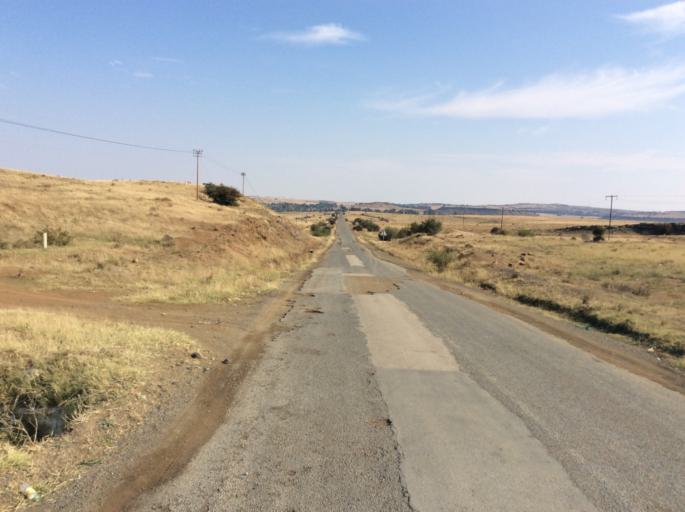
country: LS
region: Mafeteng
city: Mafeteng
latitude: -29.7194
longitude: 27.0074
